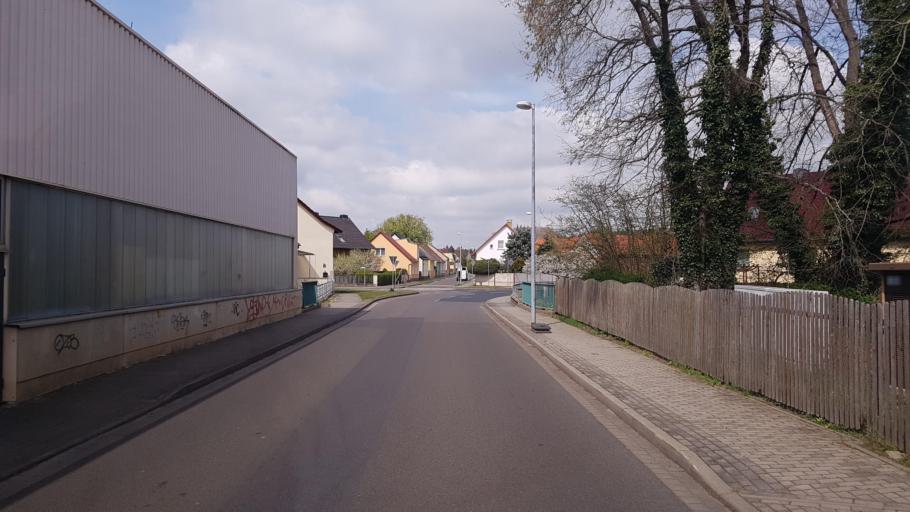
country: DE
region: Brandenburg
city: Luckenwalde
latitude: 52.1146
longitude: 13.1969
